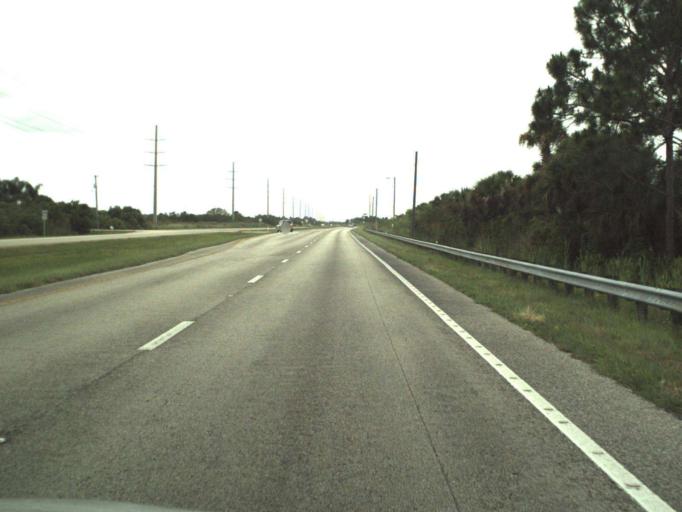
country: US
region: Florida
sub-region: Brevard County
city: Titusville
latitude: 28.5507
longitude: -80.8597
